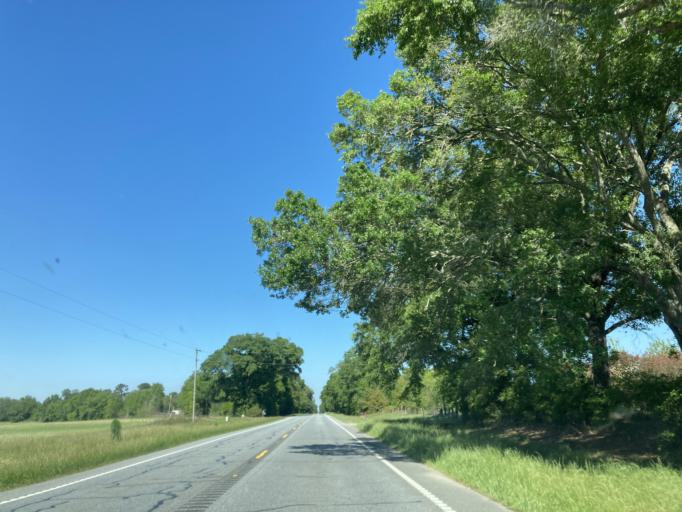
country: US
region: Georgia
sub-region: Baker County
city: Newton
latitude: 31.2533
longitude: -84.4217
